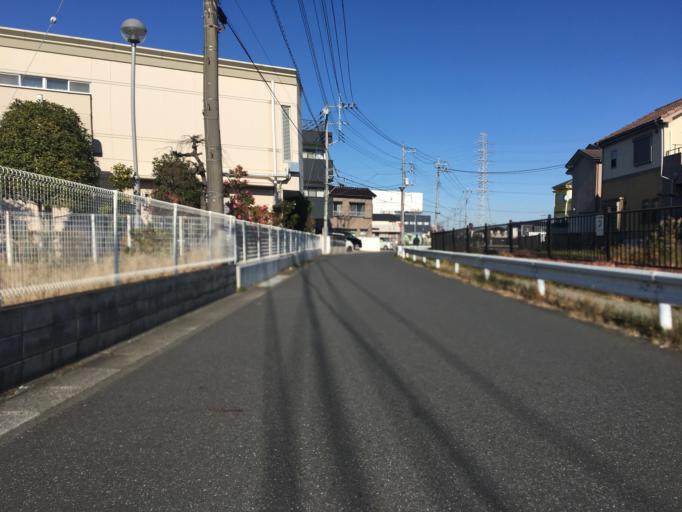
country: JP
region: Saitama
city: Yashio-shi
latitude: 35.8351
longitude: 139.8317
